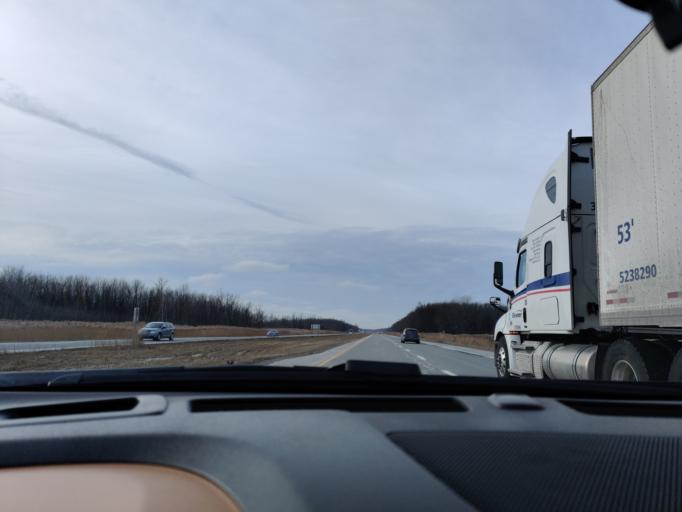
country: CA
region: Quebec
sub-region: Monteregie
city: Les Coteaux
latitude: 45.2470
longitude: -74.2642
